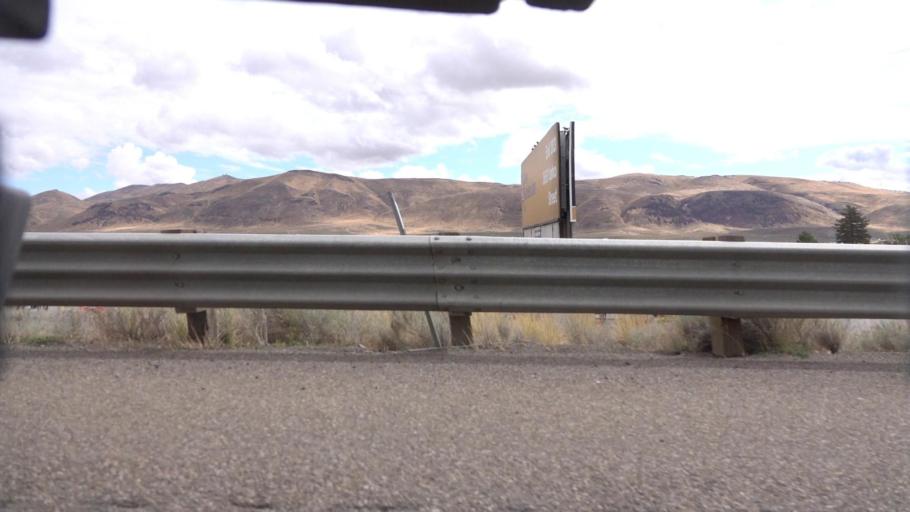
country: US
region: Nevada
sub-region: Elko County
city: Elko
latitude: 40.8898
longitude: -115.7129
